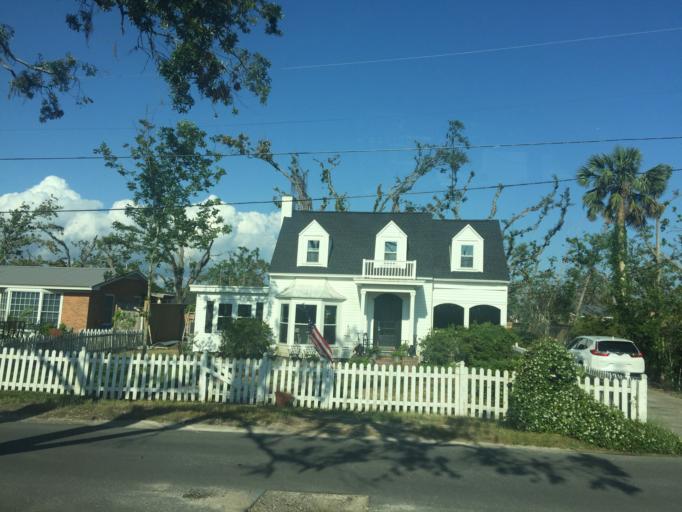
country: US
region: Florida
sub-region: Bay County
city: Panama City
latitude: 30.1451
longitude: -85.6505
